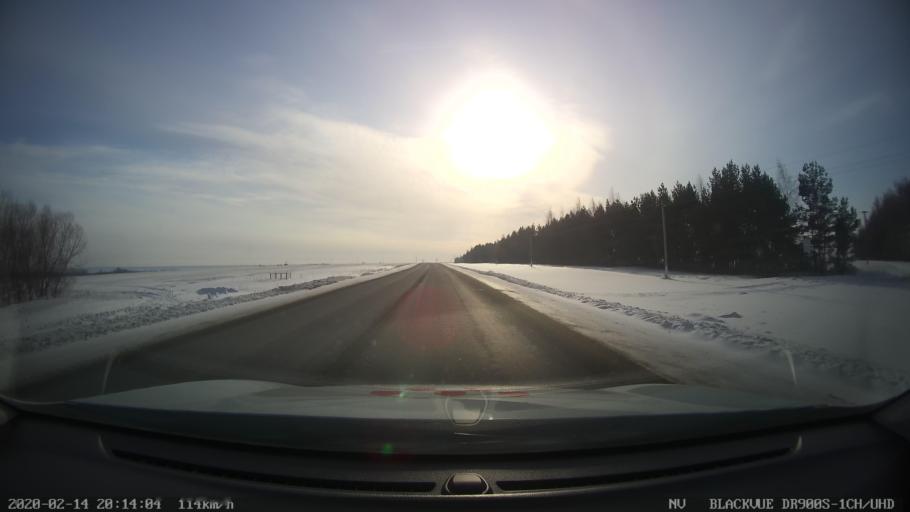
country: RU
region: Tatarstan
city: Verkhniy Uslon
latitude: 55.6499
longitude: 48.8691
